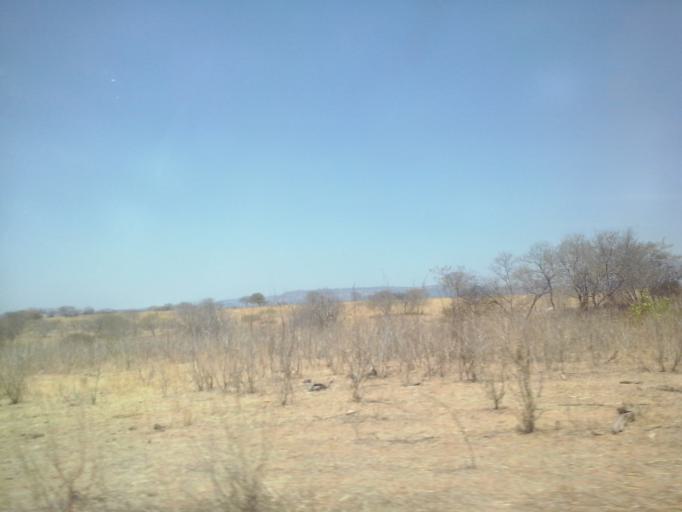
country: BR
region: Paraiba
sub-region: Paulista
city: Paulista
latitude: -6.5980
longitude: -37.6583
